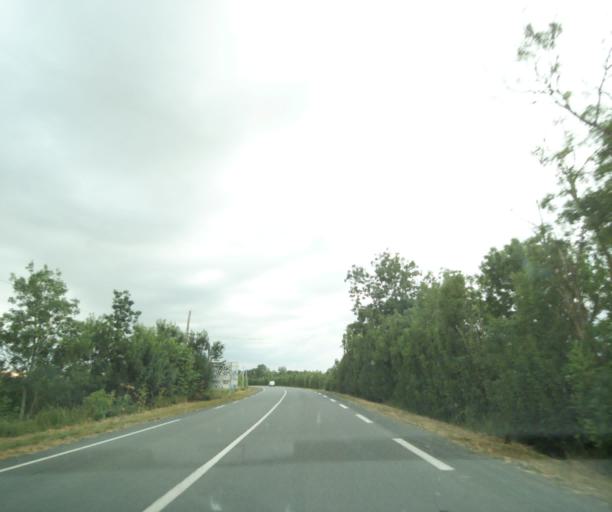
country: FR
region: Pays de la Loire
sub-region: Departement de la Vendee
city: Chaille-les-Marais
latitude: 46.4101
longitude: -1.0383
